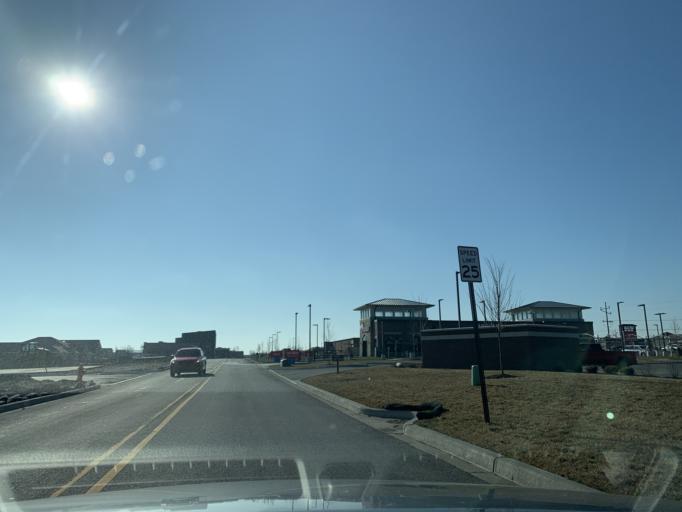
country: US
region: Indiana
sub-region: Lake County
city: Crown Point
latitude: 41.4267
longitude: -87.3341
